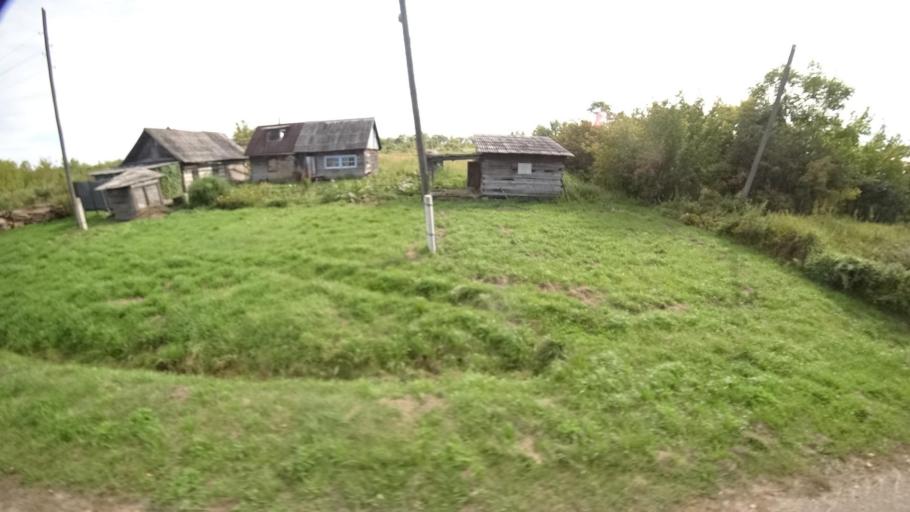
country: RU
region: Primorskiy
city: Dostoyevka
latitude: 44.3279
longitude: 133.4915
